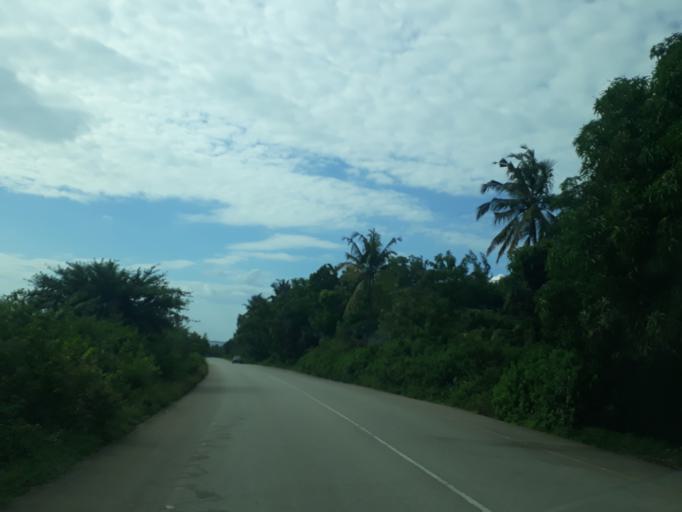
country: TZ
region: Zanzibar North
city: Kijini
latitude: -5.8457
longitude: 39.2838
